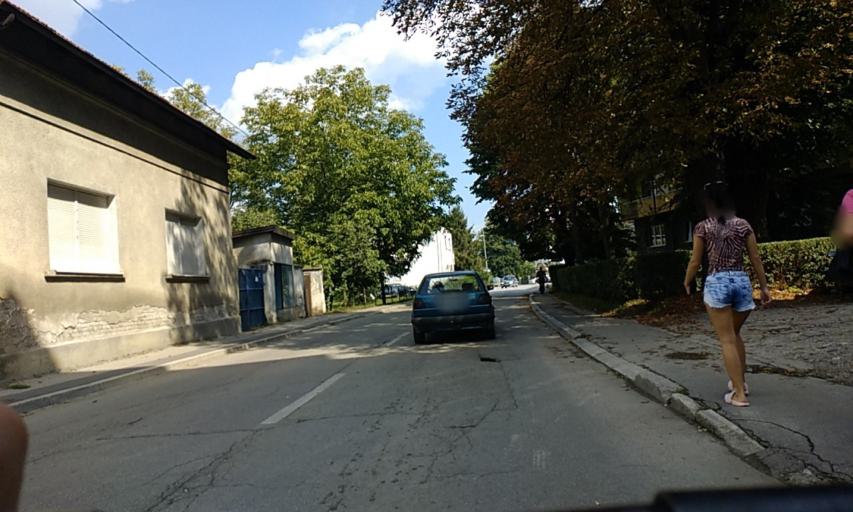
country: BA
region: Republika Srpska
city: Mejdan - Obilicevo
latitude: 44.7654
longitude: 17.1858
